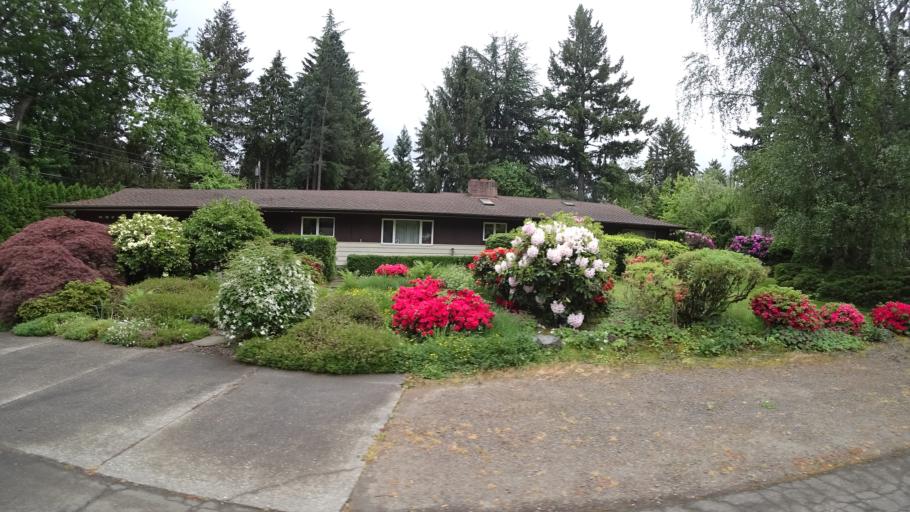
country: US
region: Oregon
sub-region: Washington County
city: Garden Home-Whitford
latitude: 45.4670
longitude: -122.7735
